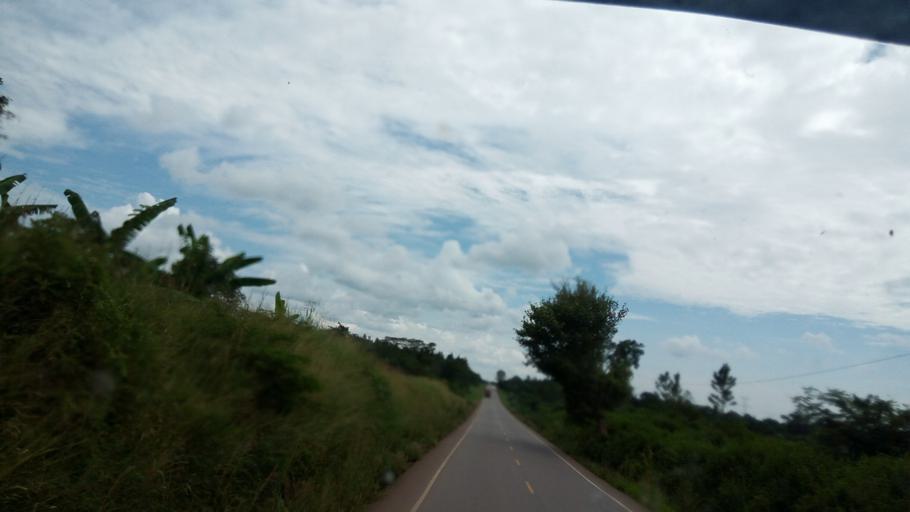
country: UG
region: Central Region
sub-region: Nakasongola District
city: Nakasongola
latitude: 1.1697
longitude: 32.4631
